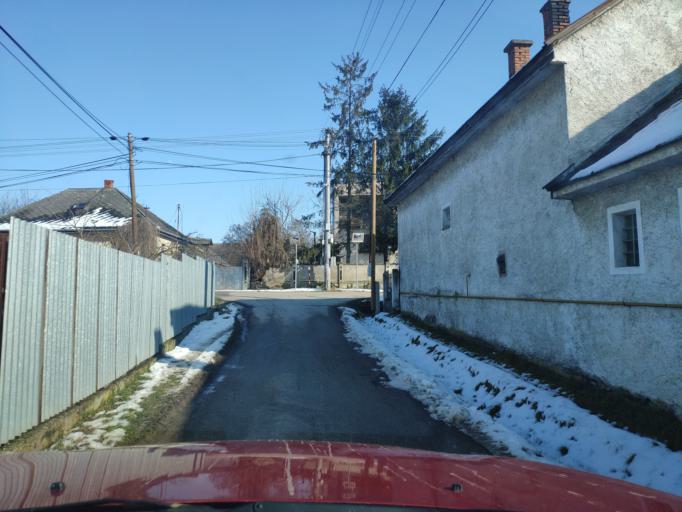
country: HU
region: Borsod-Abauj-Zemplen
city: Gonc
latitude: 48.5793
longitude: 21.2737
